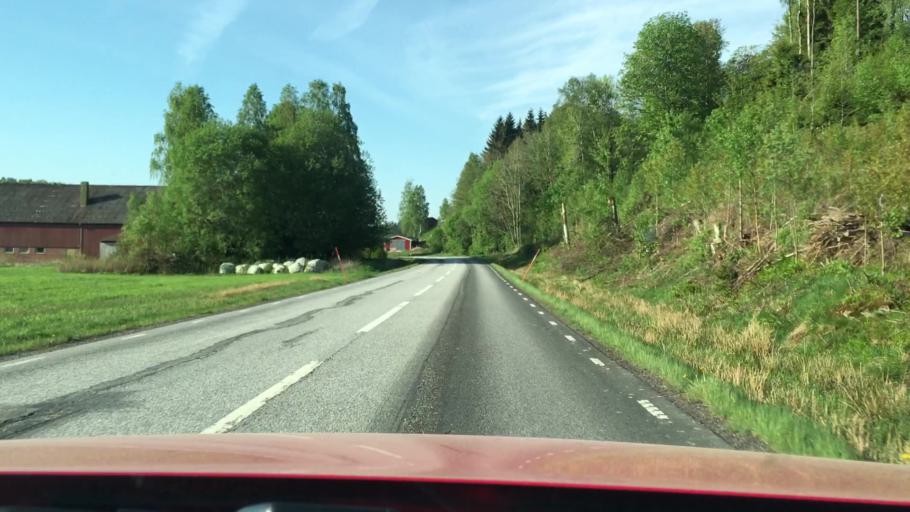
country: SE
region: Vaestra Goetaland
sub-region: Munkedals Kommun
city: Munkedal
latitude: 58.6226
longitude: 11.5589
